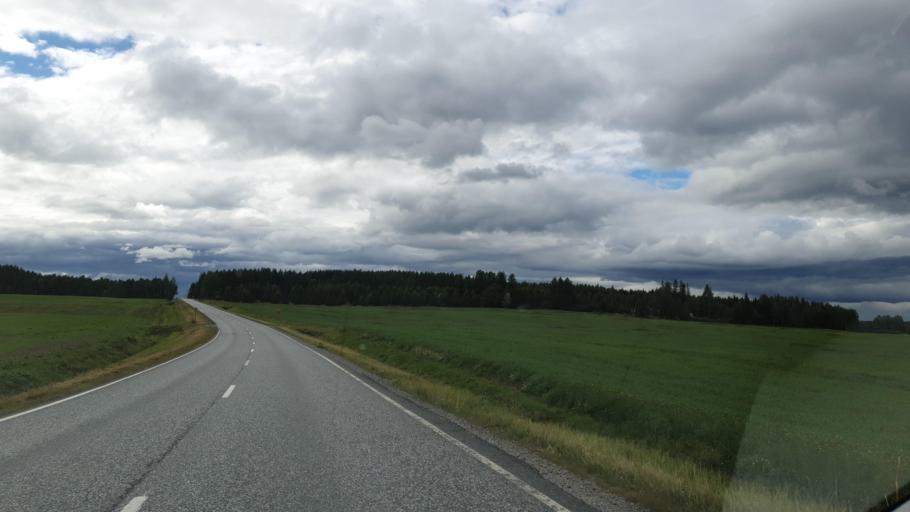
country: FI
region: Northern Savo
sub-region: Ylae-Savo
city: Iisalmi
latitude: 63.5211
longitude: 27.1901
